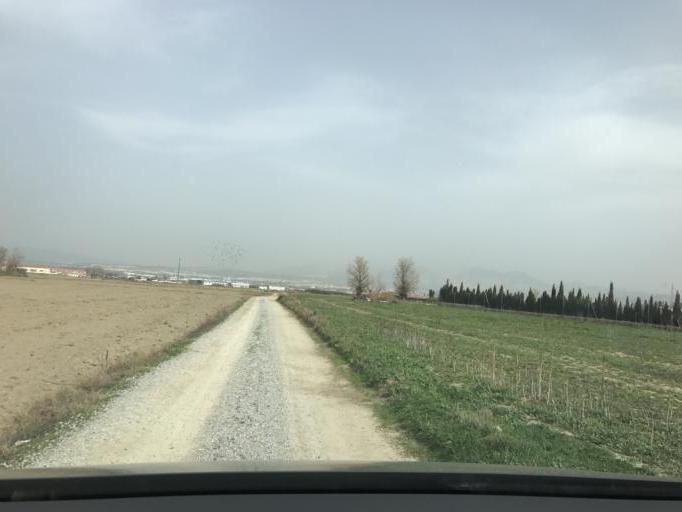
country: ES
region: Andalusia
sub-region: Provincia de Granada
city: Cullar-Vega
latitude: 37.1642
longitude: -3.6811
